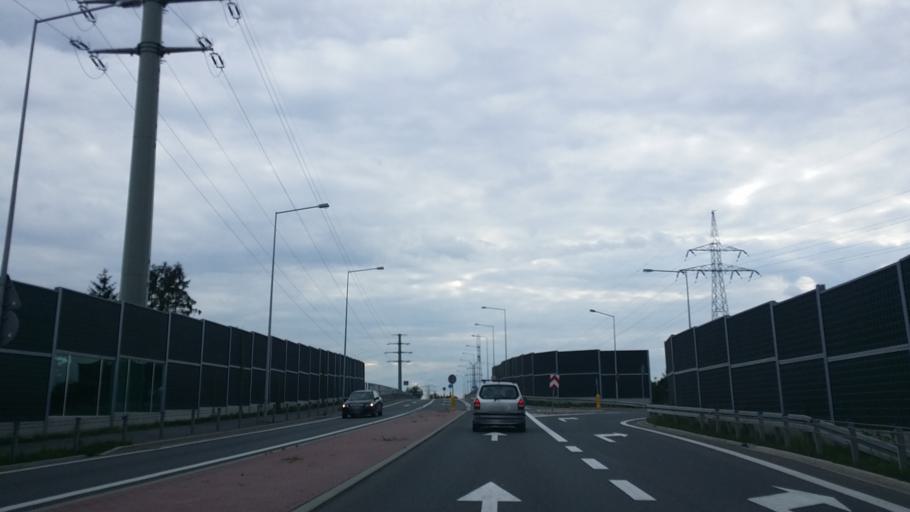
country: PL
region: Lesser Poland Voivodeship
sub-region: Powiat krakowski
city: Skawina
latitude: 49.9852
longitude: 19.8179
